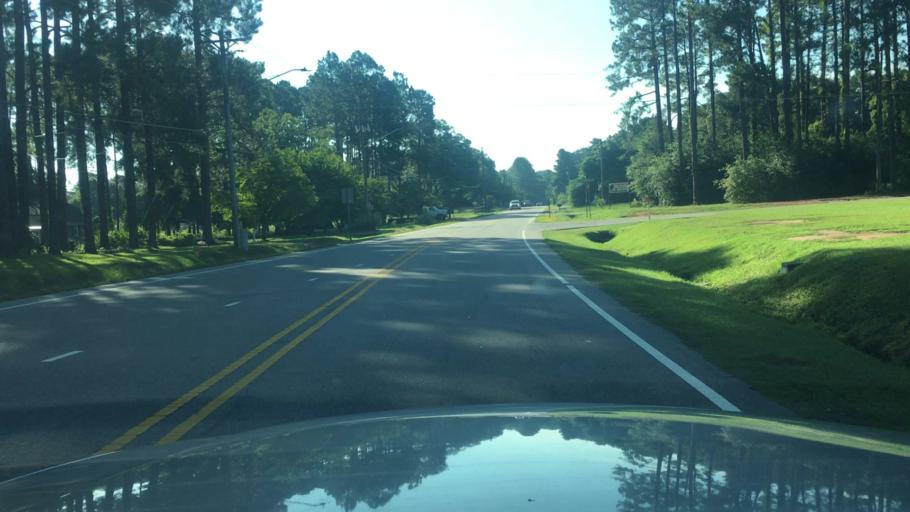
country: US
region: North Carolina
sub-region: Cumberland County
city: Fayetteville
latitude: 35.1287
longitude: -78.8940
